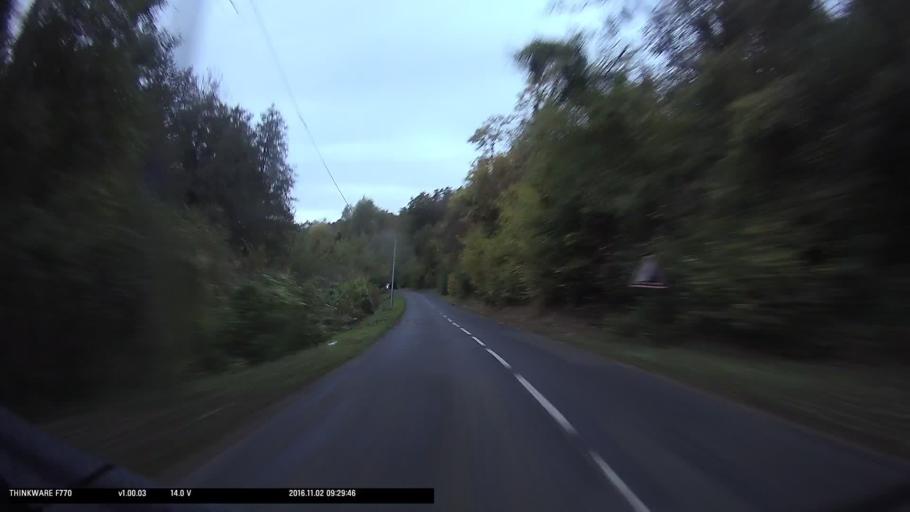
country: FR
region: Ile-de-France
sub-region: Departement du Val-d'Oise
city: Ableiges
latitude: 49.0848
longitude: 1.9988
